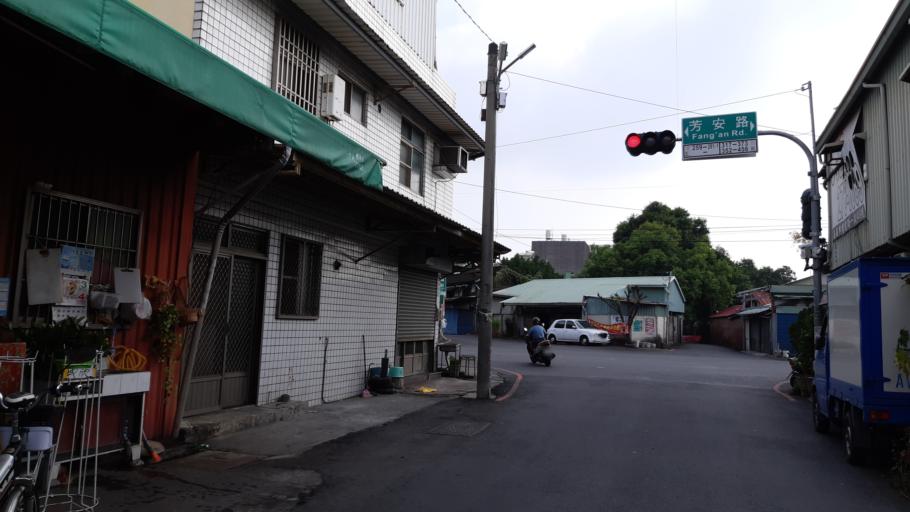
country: TW
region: Taiwan
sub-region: Chiayi
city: Jiayi Shi
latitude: 23.4685
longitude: 120.4573
